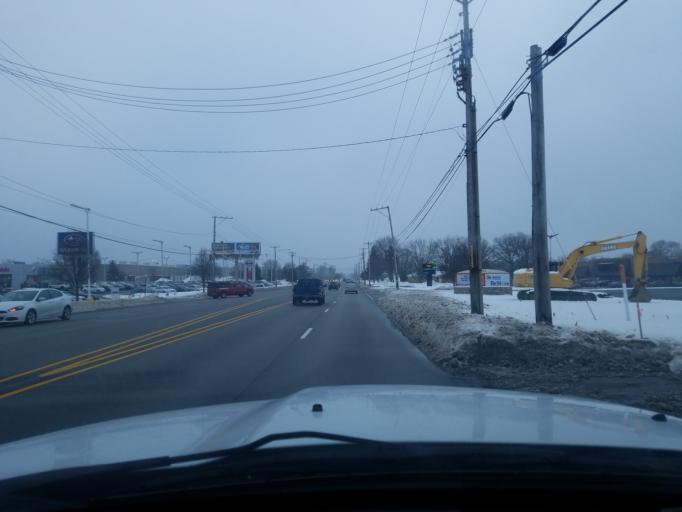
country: US
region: Indiana
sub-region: Saint Joseph County
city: Georgetown
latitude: 41.7085
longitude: -86.1876
